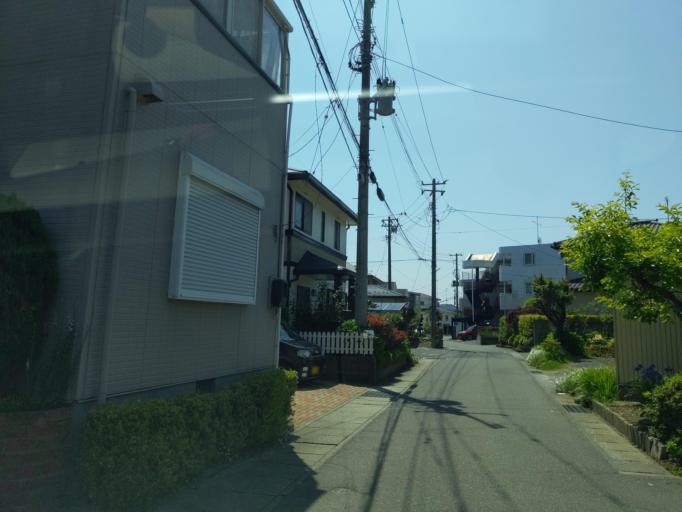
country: JP
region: Fukushima
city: Koriyama
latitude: 37.3881
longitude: 140.3454
